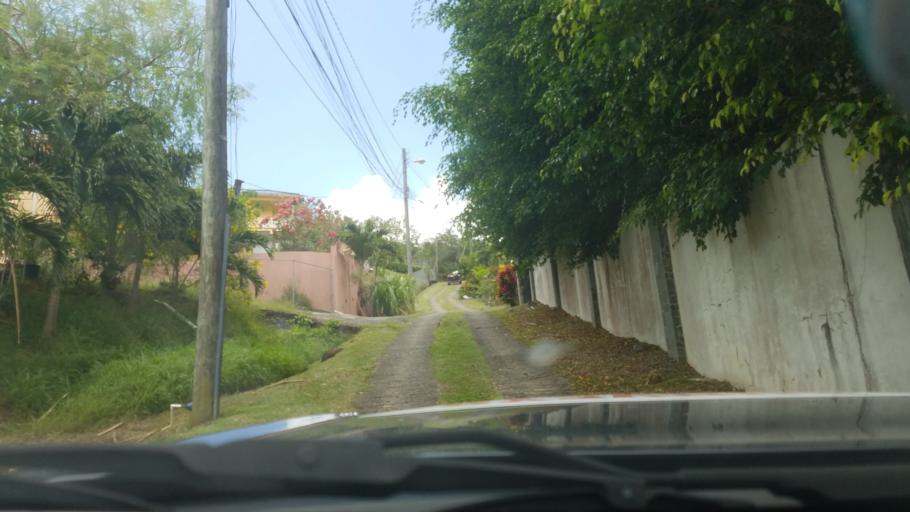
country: LC
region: Gros-Islet
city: Gros Islet
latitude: 14.0612
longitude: -60.9486
